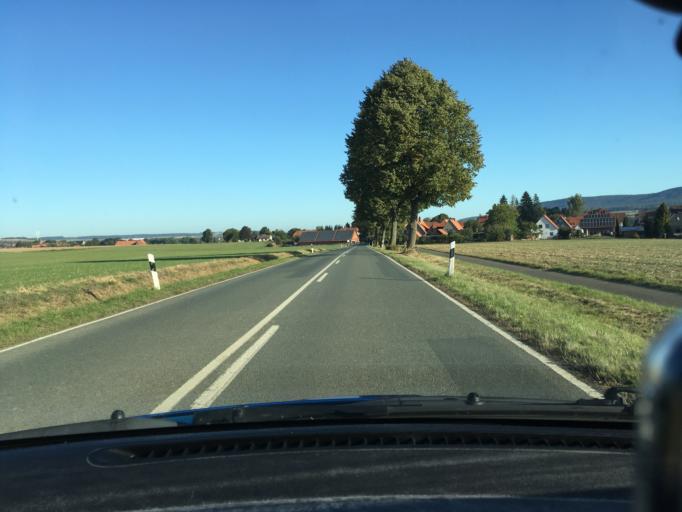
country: DE
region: Lower Saxony
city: Hulsede
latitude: 52.2367
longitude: 9.3744
